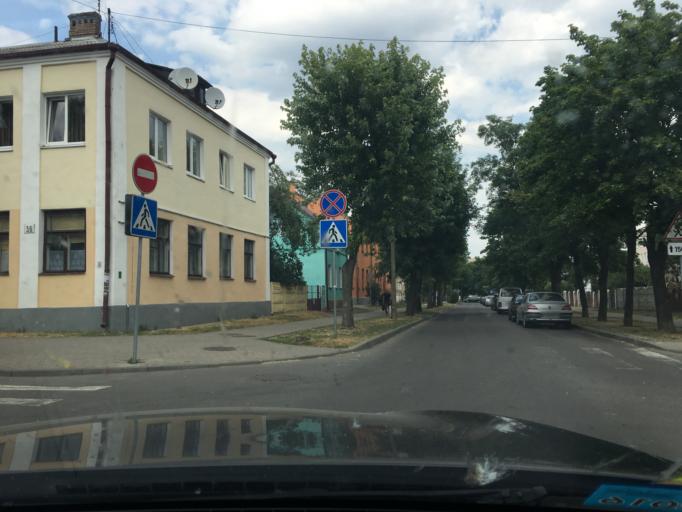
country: BY
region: Brest
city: Brest
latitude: 52.0949
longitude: 23.6935
